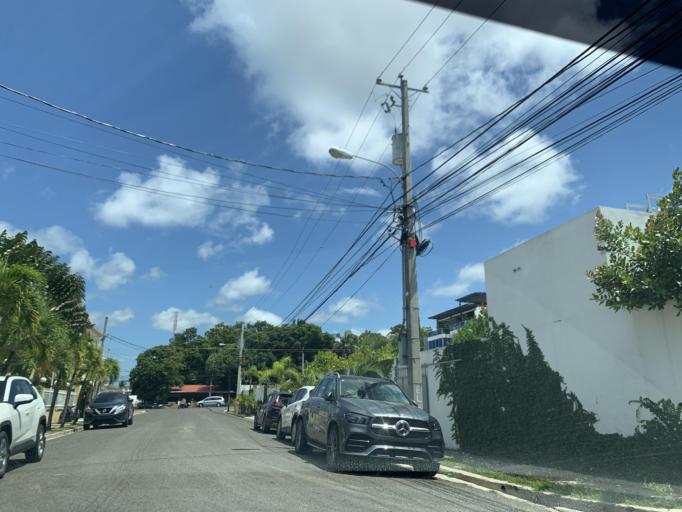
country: DO
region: Puerto Plata
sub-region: Puerto Plata
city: Puerto Plata
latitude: 19.7851
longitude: -70.6716
